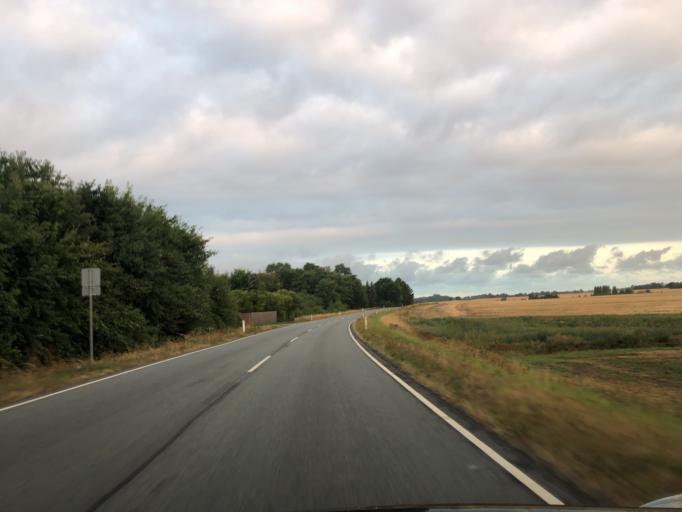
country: DK
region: Zealand
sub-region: Slagelse Kommune
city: Slagelse
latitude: 55.4336
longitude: 11.4096
